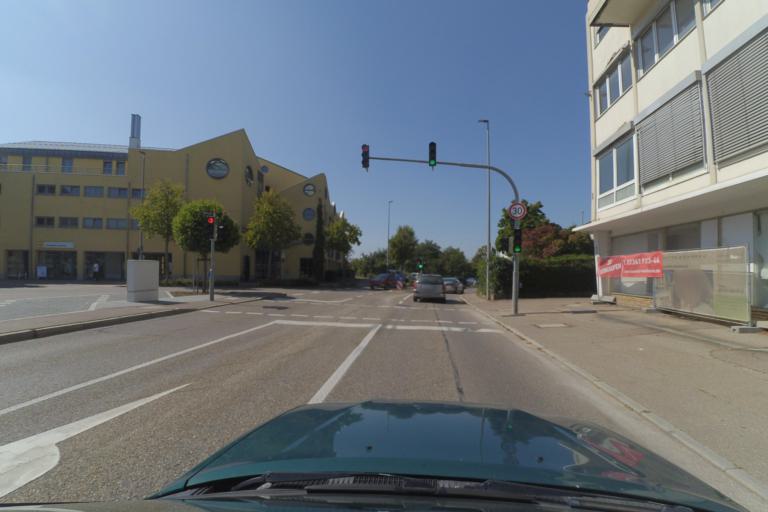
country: DE
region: Baden-Wuerttemberg
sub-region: Regierungsbezirk Stuttgart
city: Giengen an der Brenz
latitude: 48.6226
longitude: 10.2436
